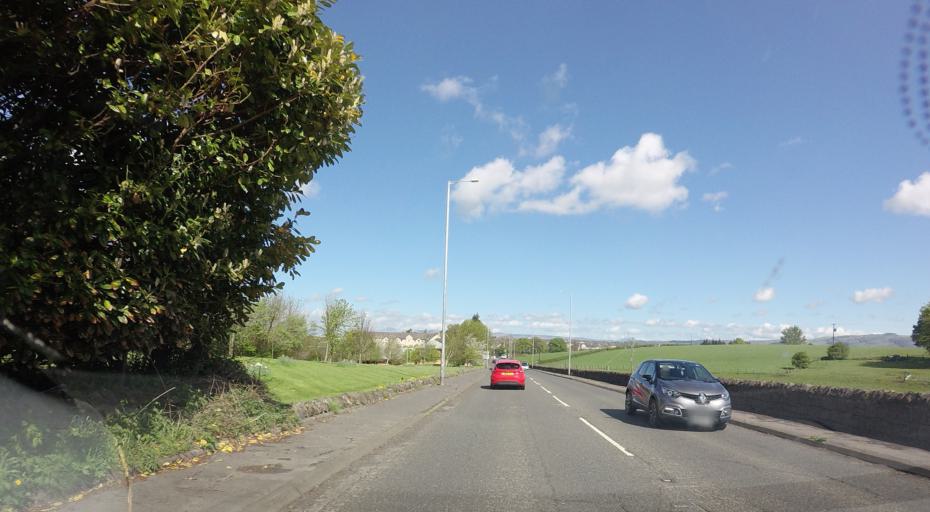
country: GB
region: Scotland
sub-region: Stirling
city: Bannockburn
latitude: 56.0822
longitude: -3.9251
